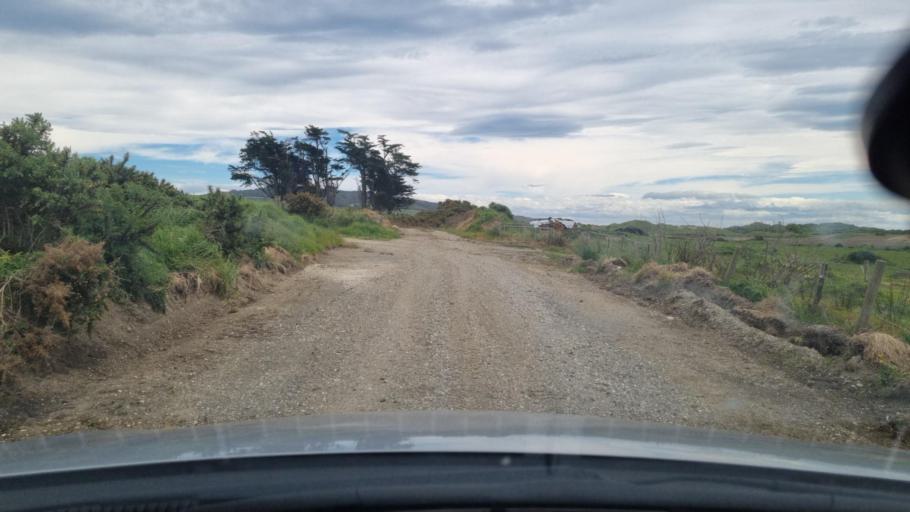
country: NZ
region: Southland
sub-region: Invercargill City
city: Bluff
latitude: -46.5201
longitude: 168.2946
